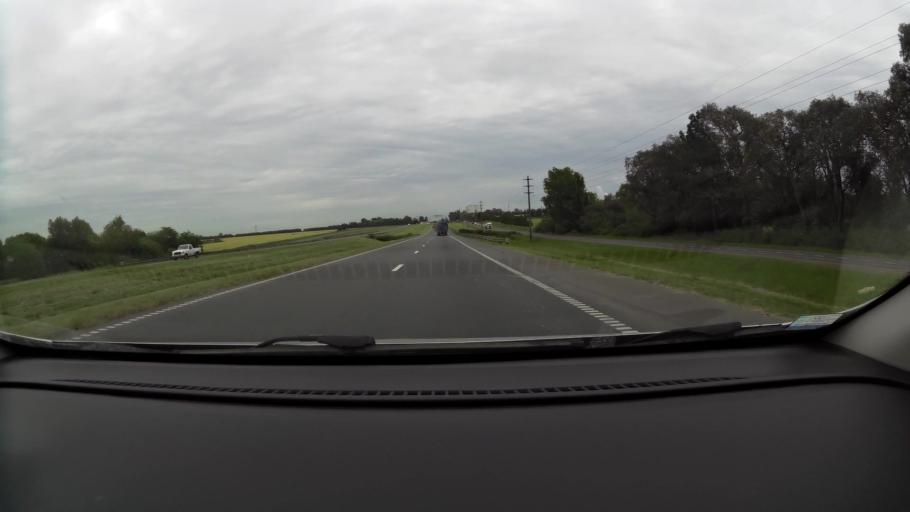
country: AR
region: Buenos Aires
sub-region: Partido de Zarate
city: Zarate
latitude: -34.1059
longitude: -59.1366
